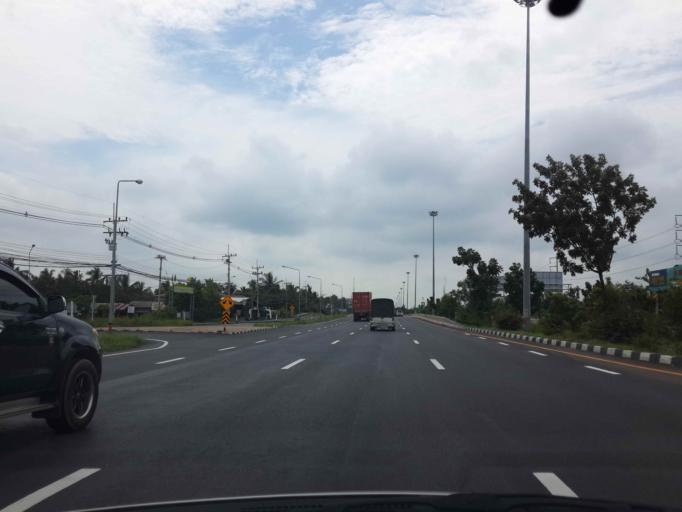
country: TH
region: Samut Songkhram
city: Samut Songkhram
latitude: 13.3971
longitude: 100.0049
